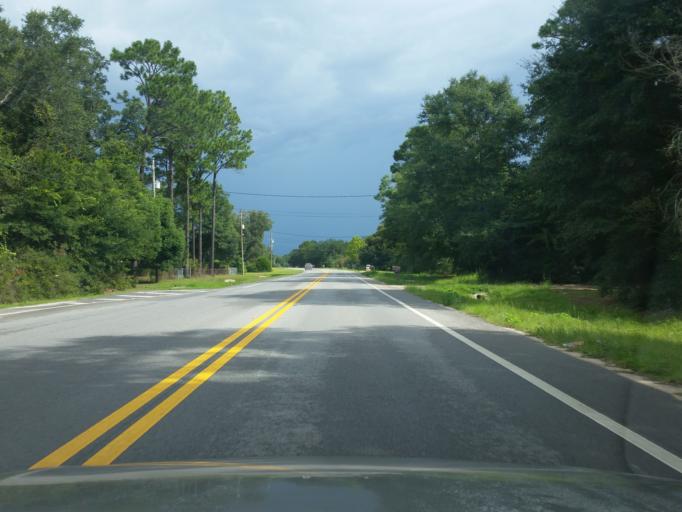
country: US
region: Florida
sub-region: Escambia County
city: Ensley
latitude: 30.5369
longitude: -87.3260
